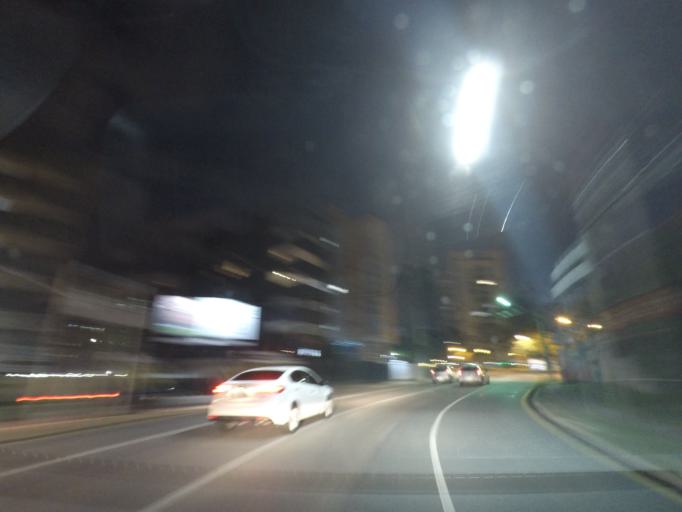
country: BR
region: Parana
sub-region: Curitiba
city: Curitiba
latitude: -25.4179
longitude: -49.2647
